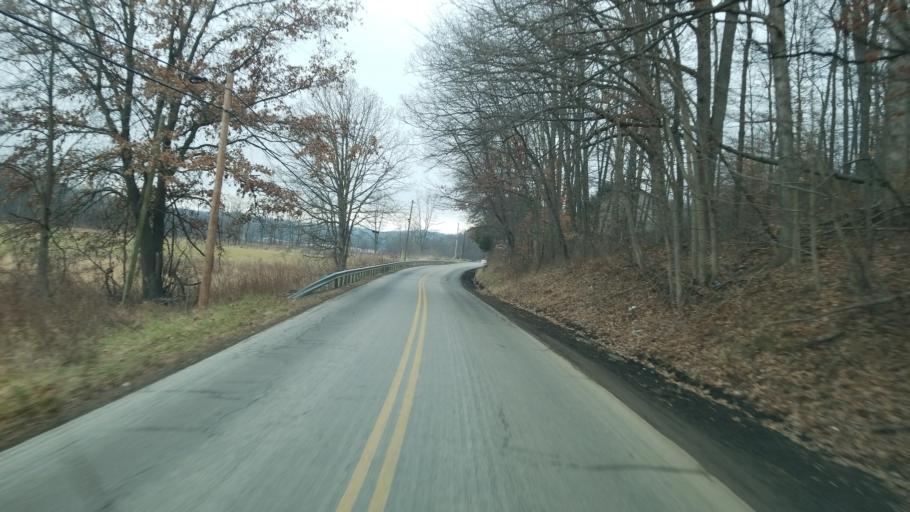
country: US
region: Ohio
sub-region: Holmes County
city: Millersburg
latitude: 40.5309
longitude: -81.9046
